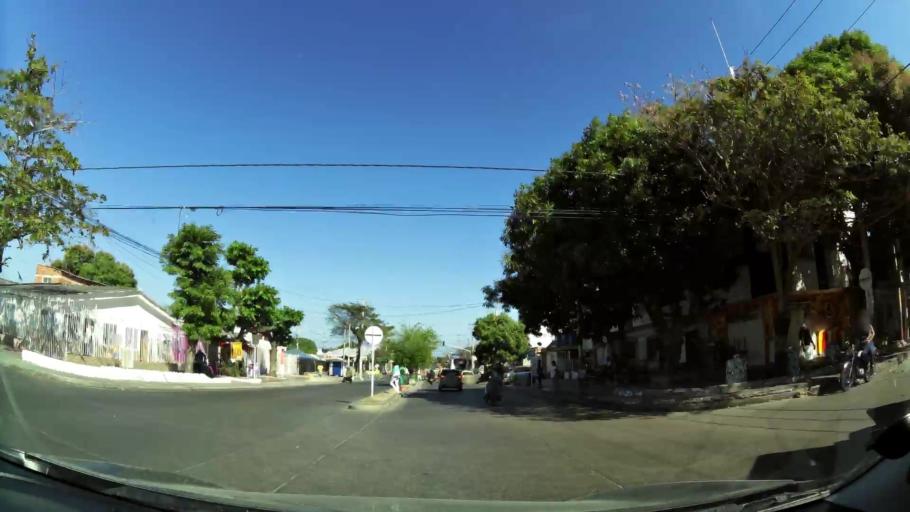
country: CO
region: Atlantico
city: Barranquilla
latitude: 10.9462
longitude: -74.8005
